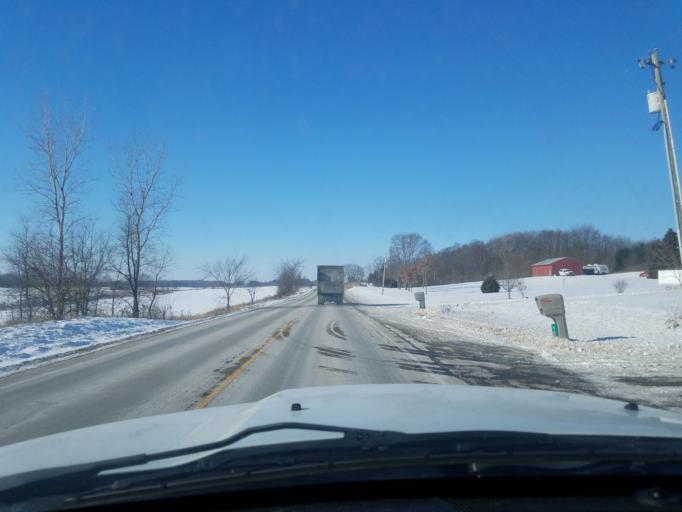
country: US
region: Indiana
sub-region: Noble County
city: Kendallville
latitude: 41.3954
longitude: -85.3345
